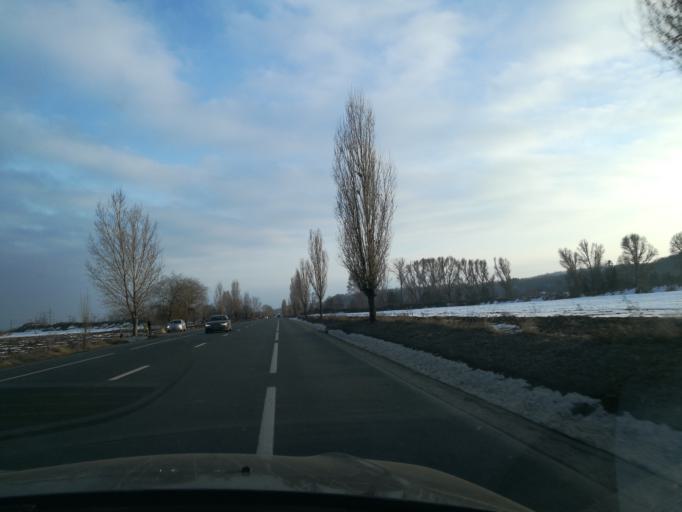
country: RO
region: Bacau
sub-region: Comuna Racaciuni
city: Racaciuni
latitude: 46.3547
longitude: 26.9928
